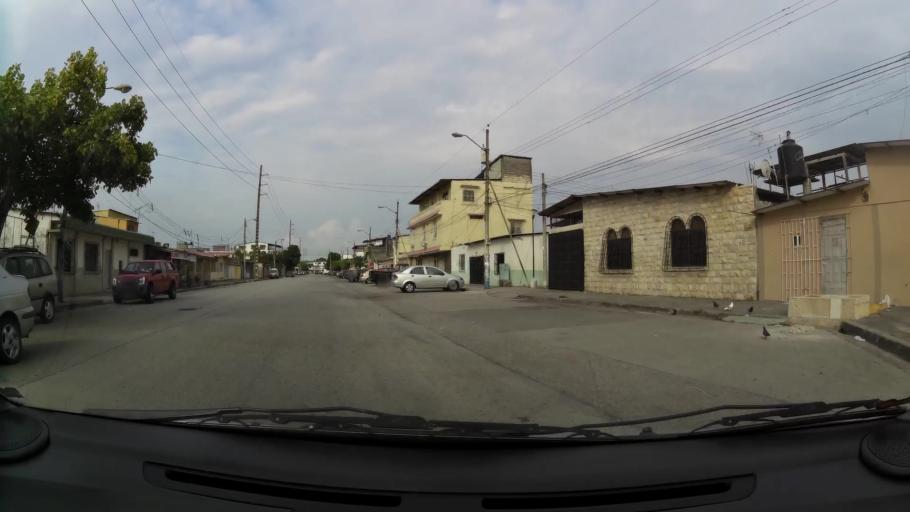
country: EC
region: Guayas
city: Guayaquil
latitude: -2.2499
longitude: -79.9022
